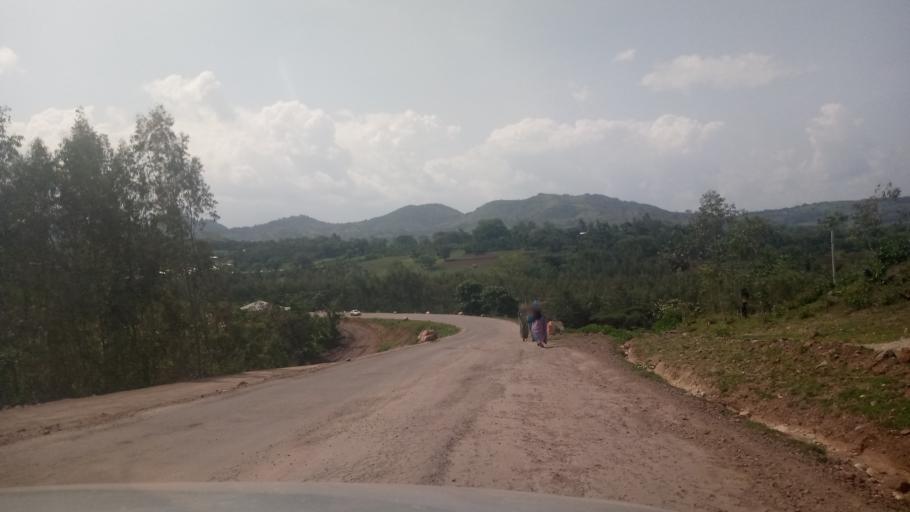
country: ET
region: Oromiya
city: Agaro
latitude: 7.9937
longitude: 36.5042
